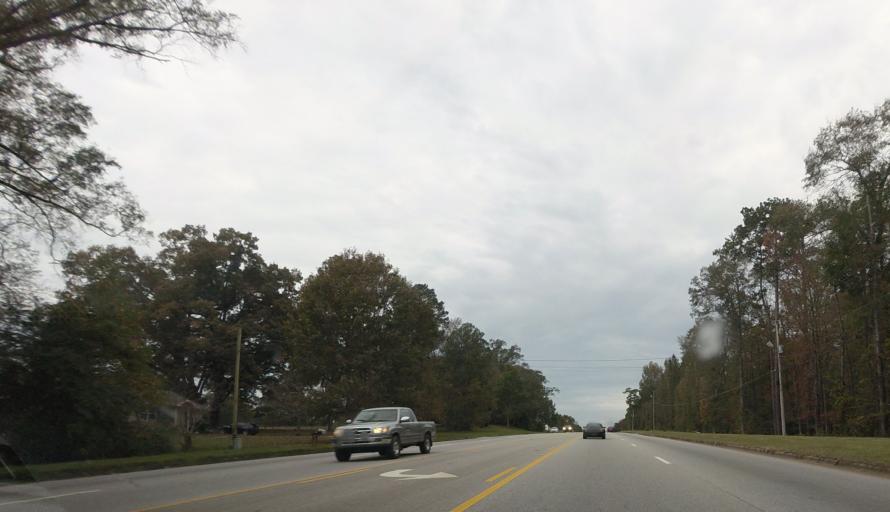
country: US
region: Alabama
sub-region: Lee County
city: Opelika
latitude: 32.6418
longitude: -85.3273
